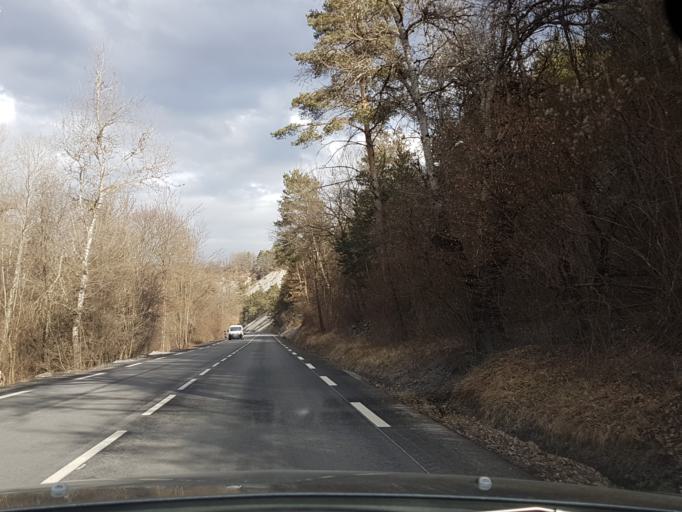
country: FR
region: Provence-Alpes-Cote d'Azur
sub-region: Departement des Hautes-Alpes
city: Tallard
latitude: 44.5120
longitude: 6.0643
